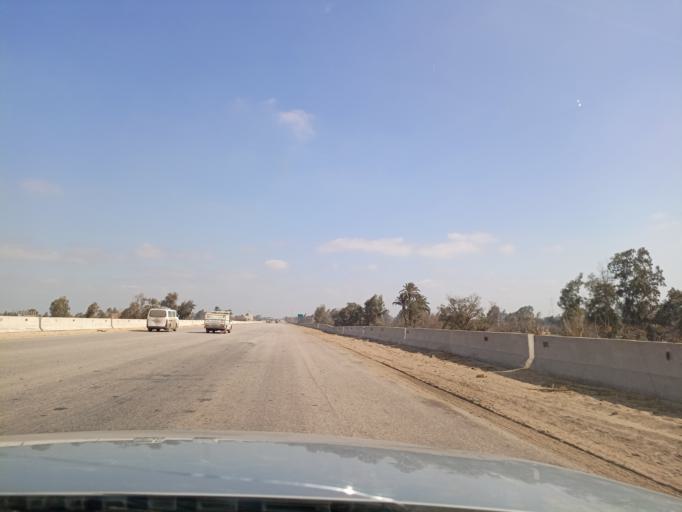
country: EG
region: Muhafazat al Minufiyah
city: Al Bajur
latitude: 30.4254
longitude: 31.0920
